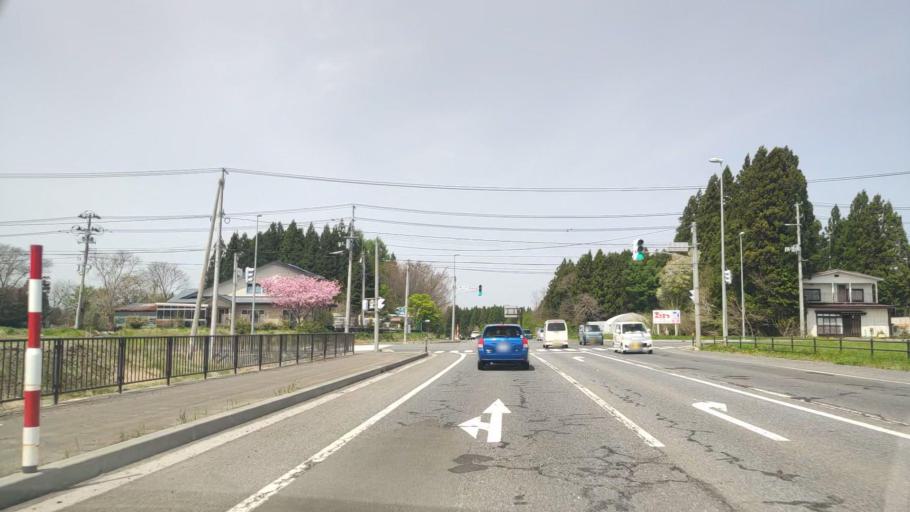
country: JP
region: Aomori
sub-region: Misawa Shi
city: Inuotose
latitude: 40.7078
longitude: 141.1611
